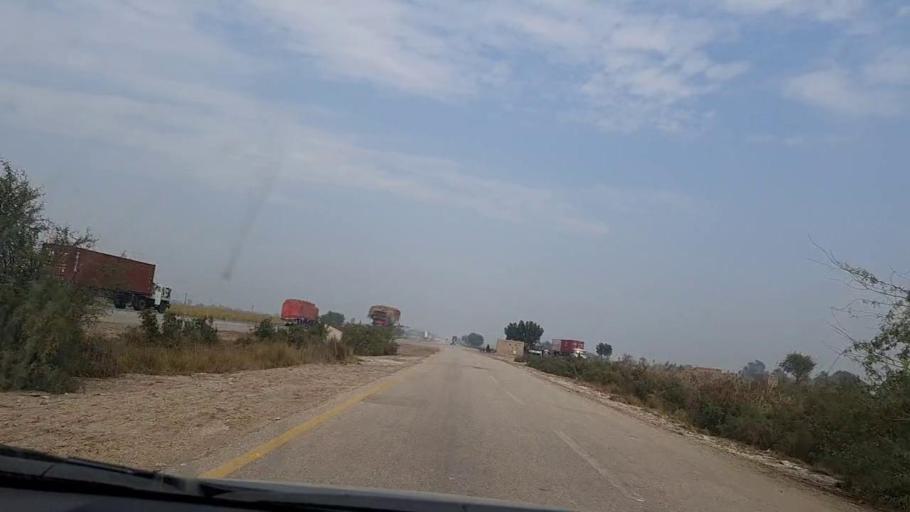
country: PK
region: Sindh
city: Daulatpur
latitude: 26.5271
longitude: 67.9733
